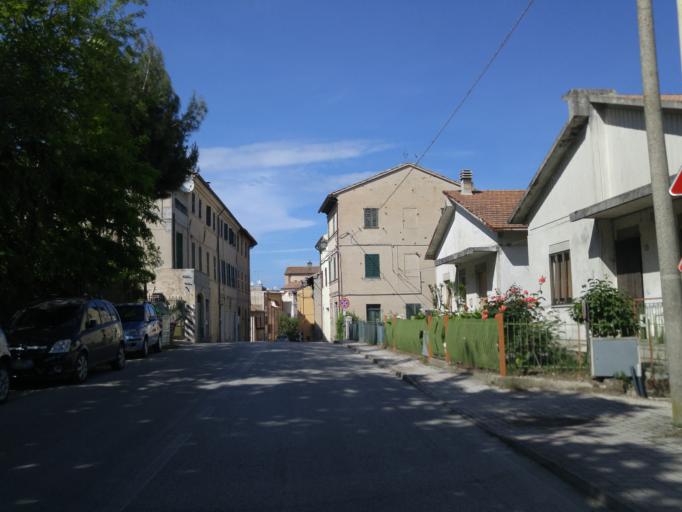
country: IT
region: The Marches
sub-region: Provincia di Pesaro e Urbino
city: San Costanzo
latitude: 43.7611
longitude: 13.0676
